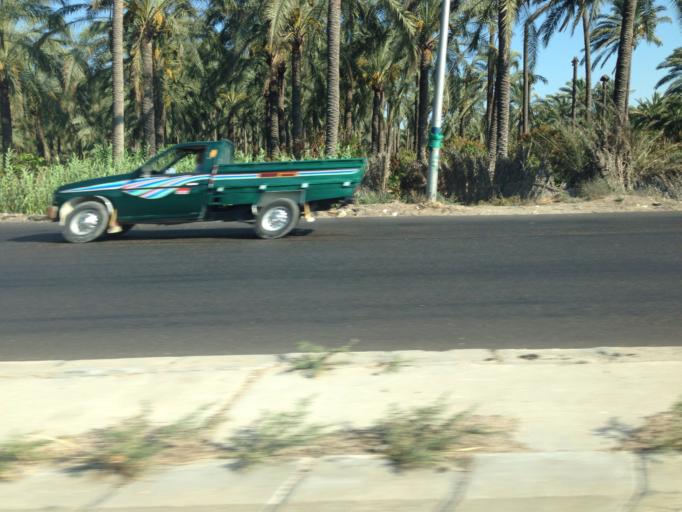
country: EG
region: Al Buhayrah
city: Idku
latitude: 31.2911
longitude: 30.2517
